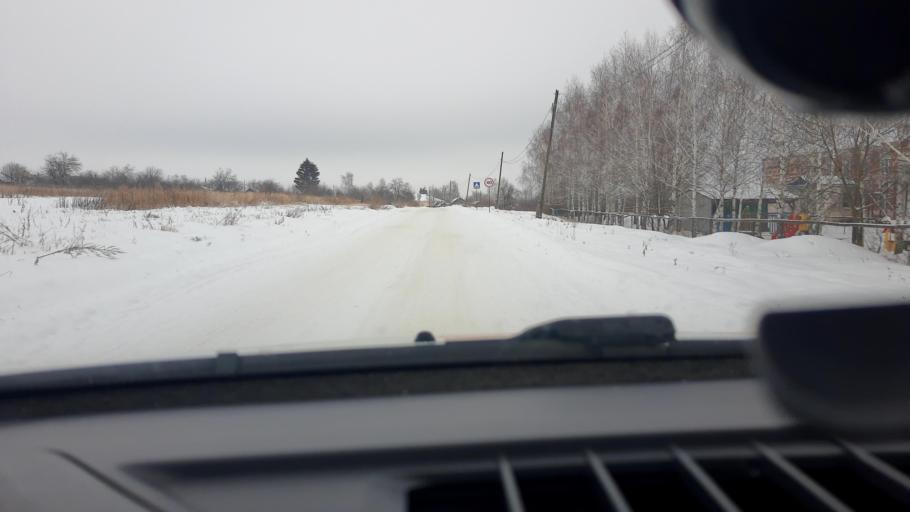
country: RU
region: Nizjnij Novgorod
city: Dal'neye Konstantinovo
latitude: 55.9247
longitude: 44.0534
